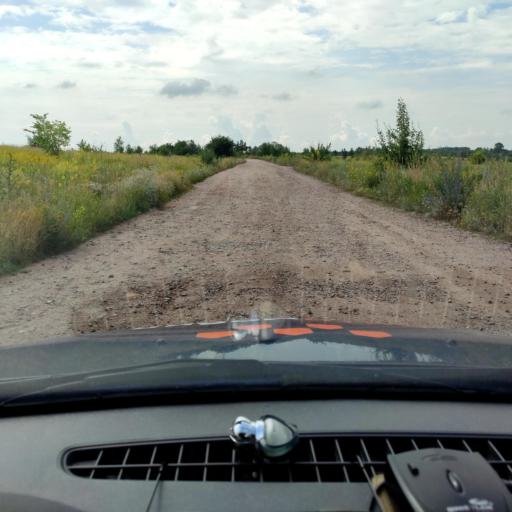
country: RU
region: Voronezj
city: Ramon'
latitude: 52.0726
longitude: 39.3233
